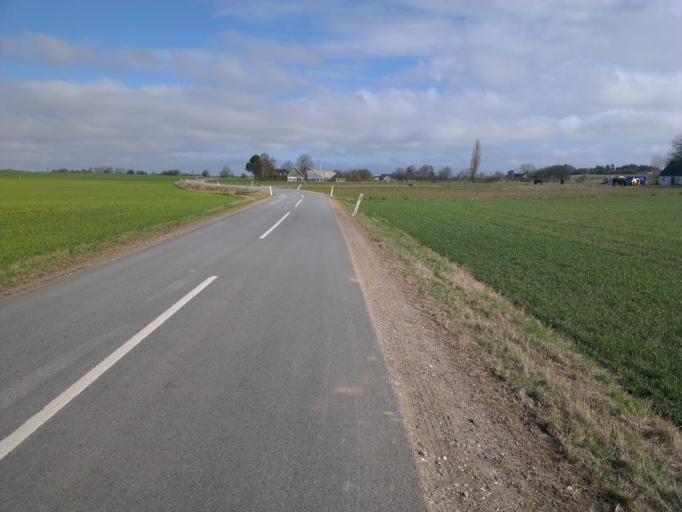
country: DK
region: Capital Region
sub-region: Hillerod Kommune
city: Skaevinge
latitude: 55.8682
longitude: 12.1149
